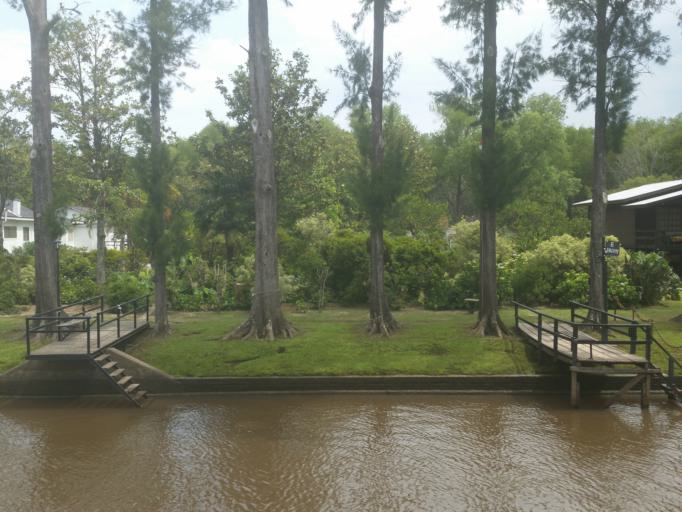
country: AR
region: Buenos Aires
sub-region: Partido de Tigre
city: Tigre
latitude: -34.3857
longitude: -58.5662
